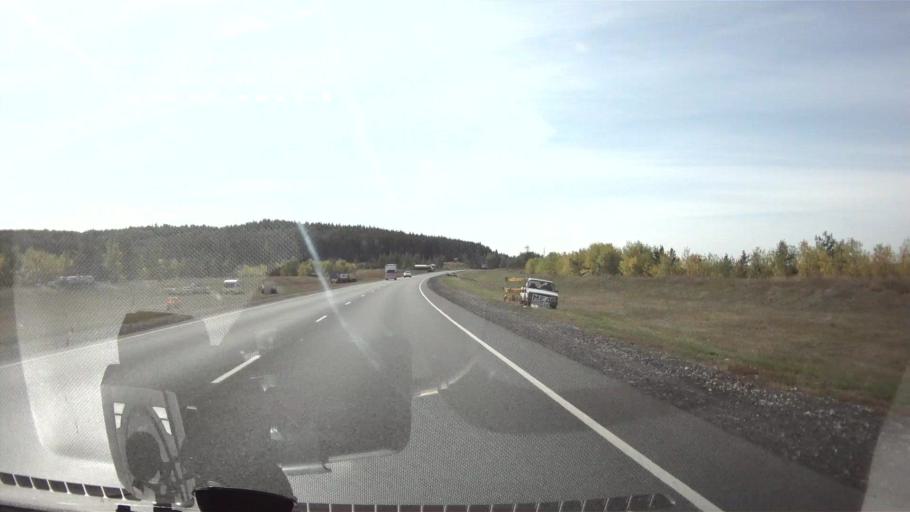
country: RU
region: Saratov
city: Khvalynsk
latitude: 52.5455
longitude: 48.0667
